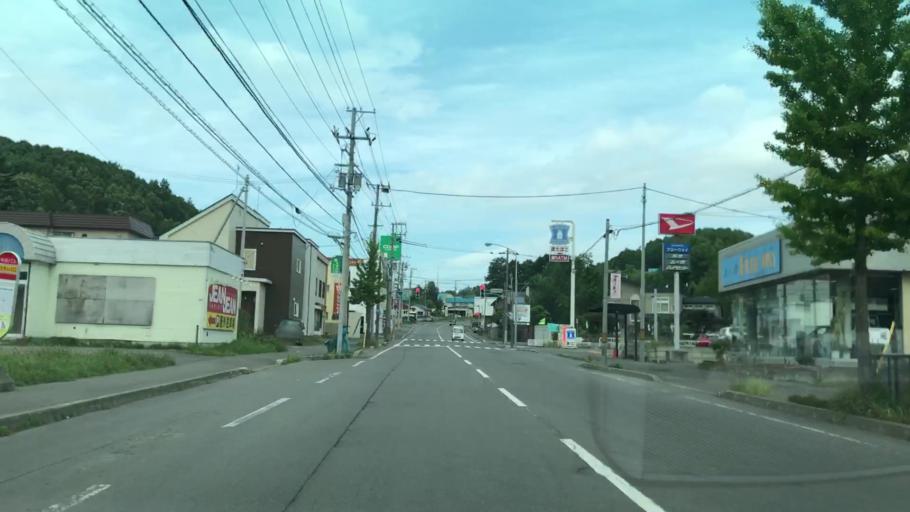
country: JP
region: Hokkaido
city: Otaru
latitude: 43.2137
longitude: 140.9613
